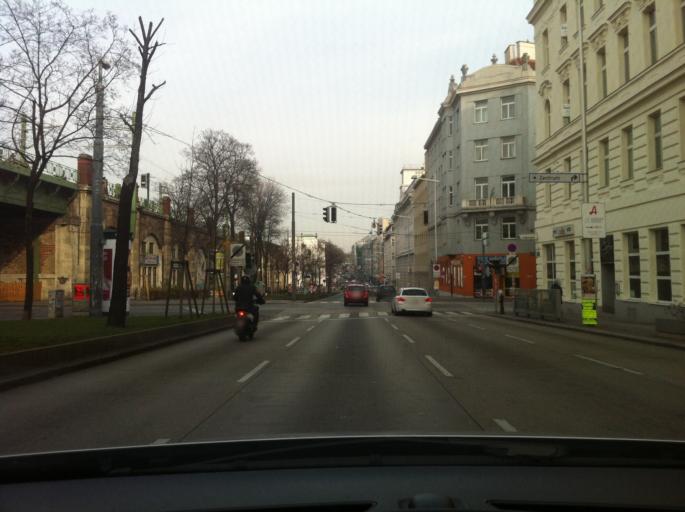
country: AT
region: Vienna
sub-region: Wien Stadt
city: Vienna
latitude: 48.2147
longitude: 16.3410
